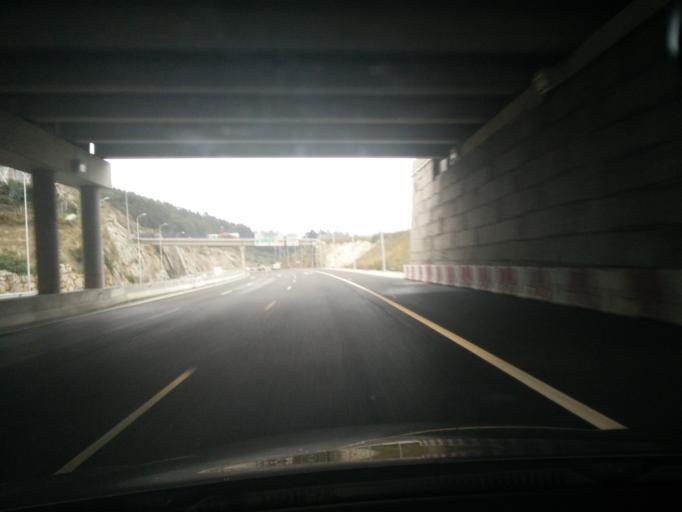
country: ES
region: Galicia
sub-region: Provincia da Coruna
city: A Coruna
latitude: 43.3402
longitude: -8.4265
